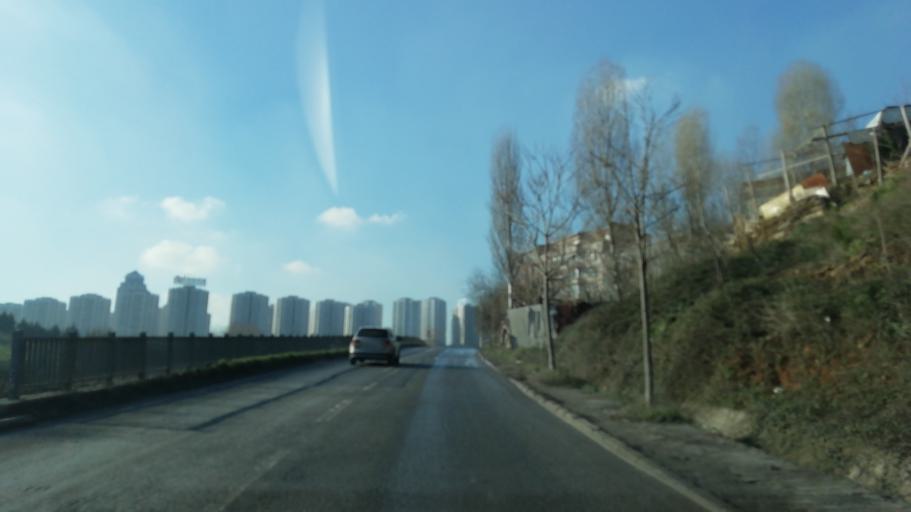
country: TR
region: Istanbul
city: Sultangazi
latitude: 41.0934
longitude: 28.9092
